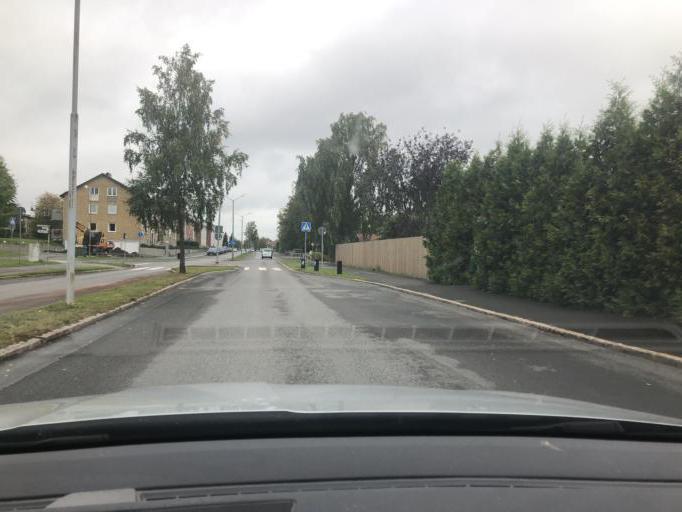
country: SE
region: Joenkoeping
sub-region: Varnamo Kommun
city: Varnamo
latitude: 57.1776
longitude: 14.0327
